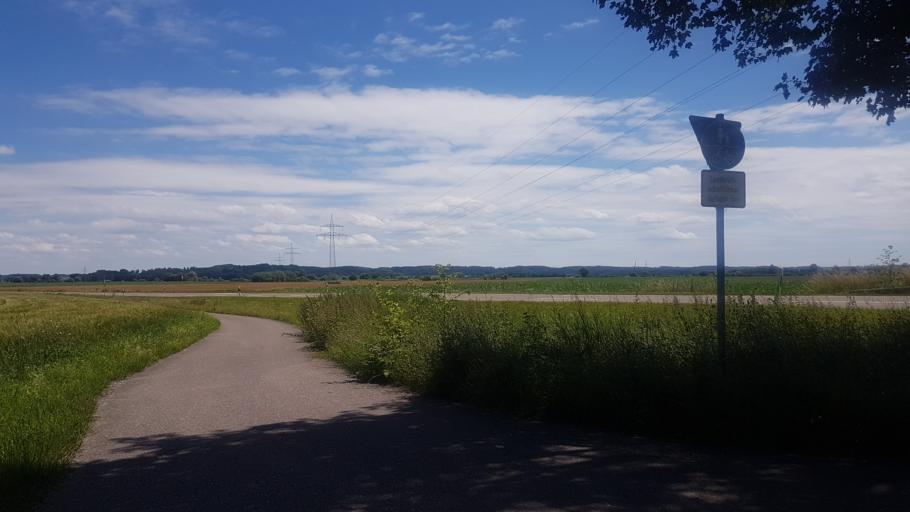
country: DE
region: Bavaria
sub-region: Swabia
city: Schwenningen
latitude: 48.6297
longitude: 10.6544
